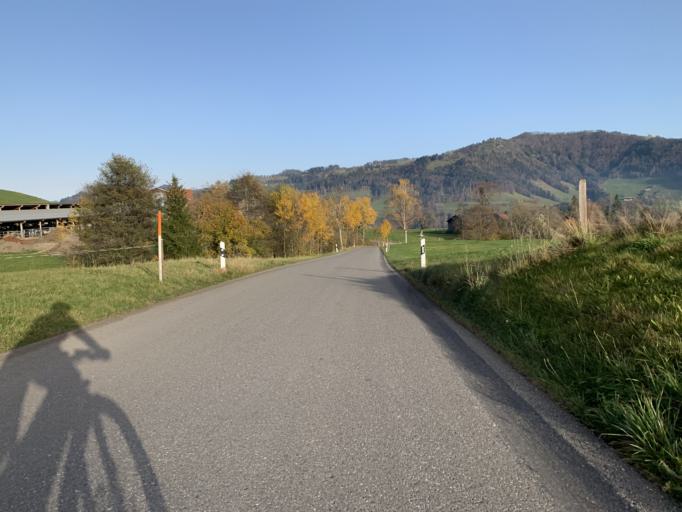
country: CH
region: Zurich
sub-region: Bezirk Hinwil
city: Wald
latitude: 47.3112
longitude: 8.8979
